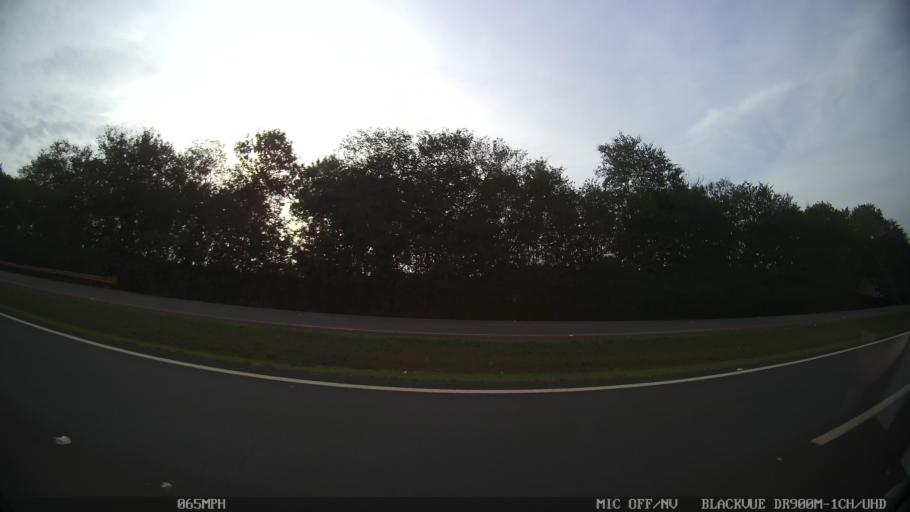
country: BR
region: Sao Paulo
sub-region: Iracemapolis
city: Iracemapolis
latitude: -22.6633
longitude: -47.5319
